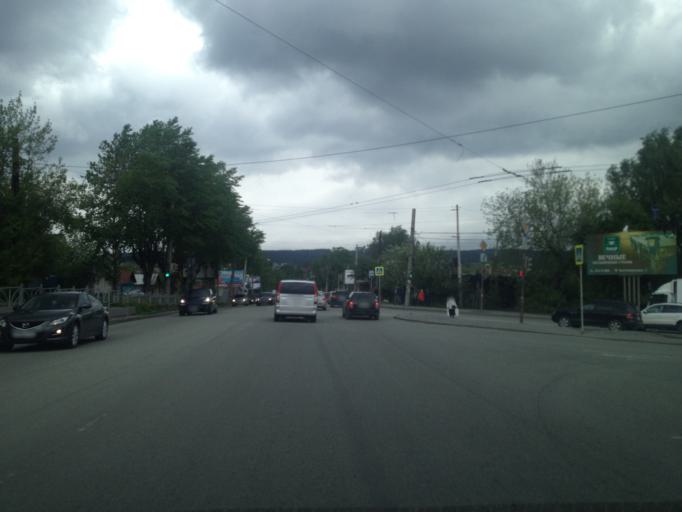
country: RU
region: Sverdlovsk
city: Istok
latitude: 56.7465
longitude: 60.6882
